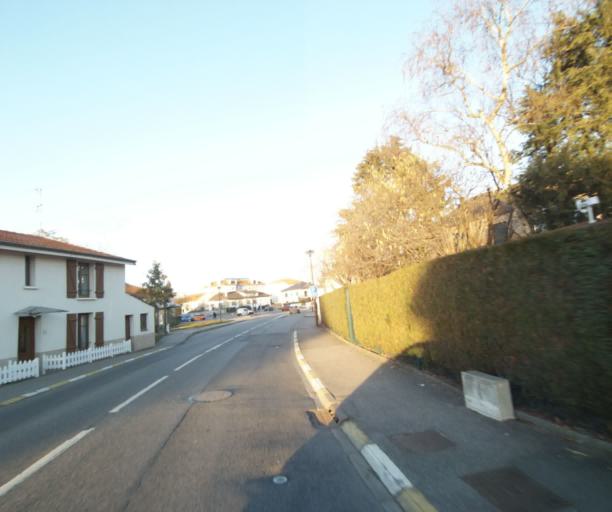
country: FR
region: Lorraine
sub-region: Departement de Meurthe-et-Moselle
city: Pulnoy
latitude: 48.7016
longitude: 6.2573
